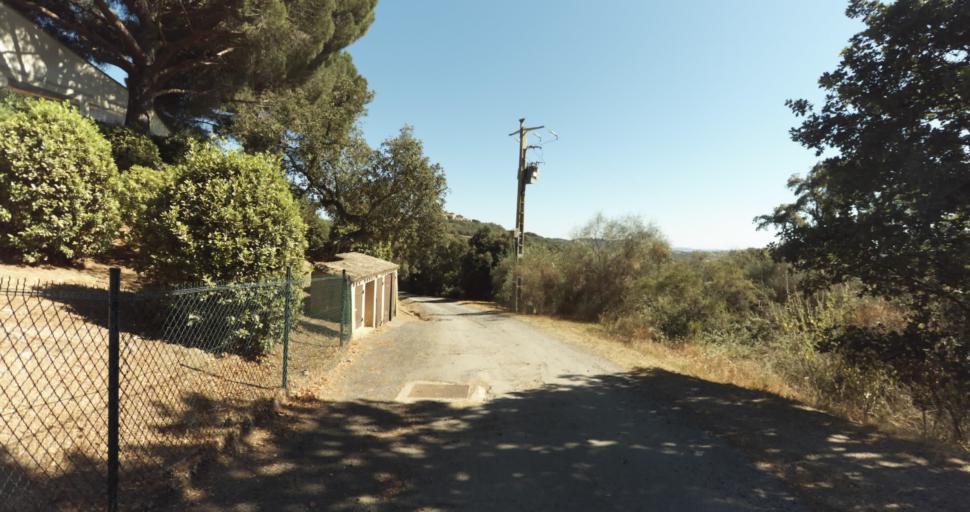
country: FR
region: Provence-Alpes-Cote d'Azur
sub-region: Departement du Var
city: Gassin
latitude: 43.2368
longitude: 6.5843
